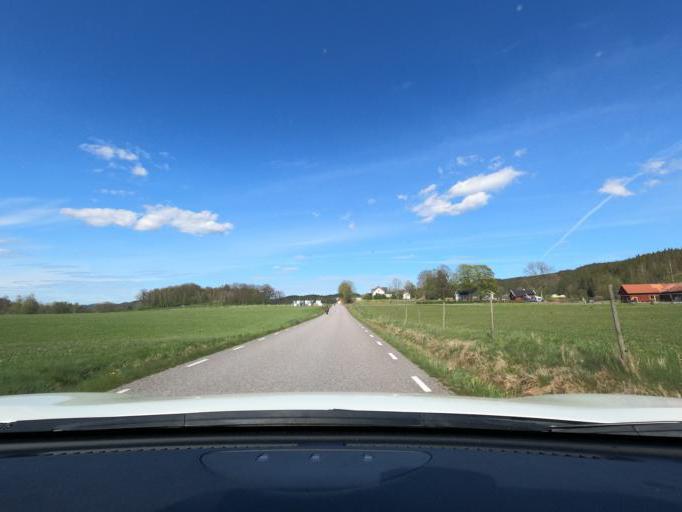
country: SE
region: Vaestra Goetaland
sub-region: Harryda Kommun
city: Ravlanda
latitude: 57.6079
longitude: 12.4814
